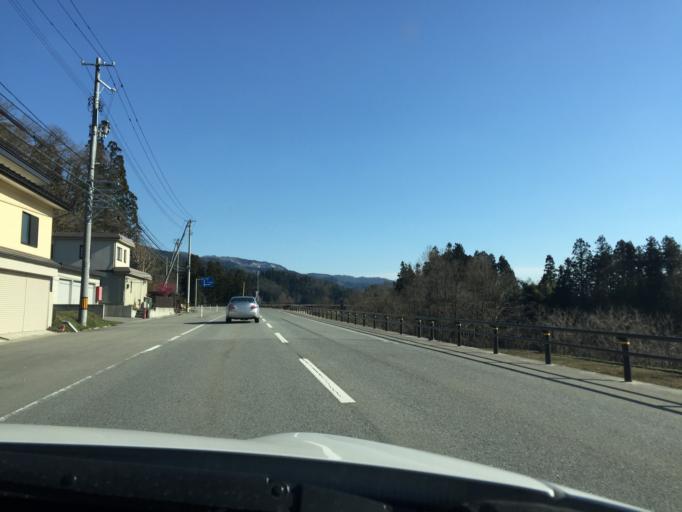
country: JP
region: Yamagata
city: Nagai
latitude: 38.2070
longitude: 140.1013
